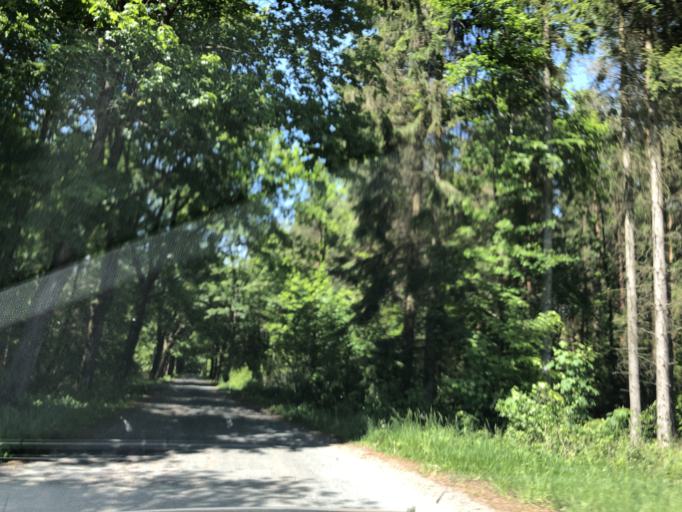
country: PL
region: West Pomeranian Voivodeship
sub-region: Powiat kolobrzeski
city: Goscino
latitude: 54.0239
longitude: 15.7392
